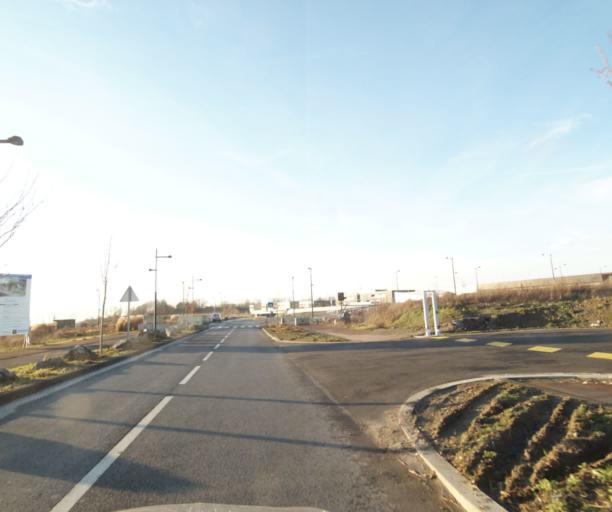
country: FR
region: Nord-Pas-de-Calais
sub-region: Departement du Nord
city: Famars
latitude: 50.3177
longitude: 3.5128
